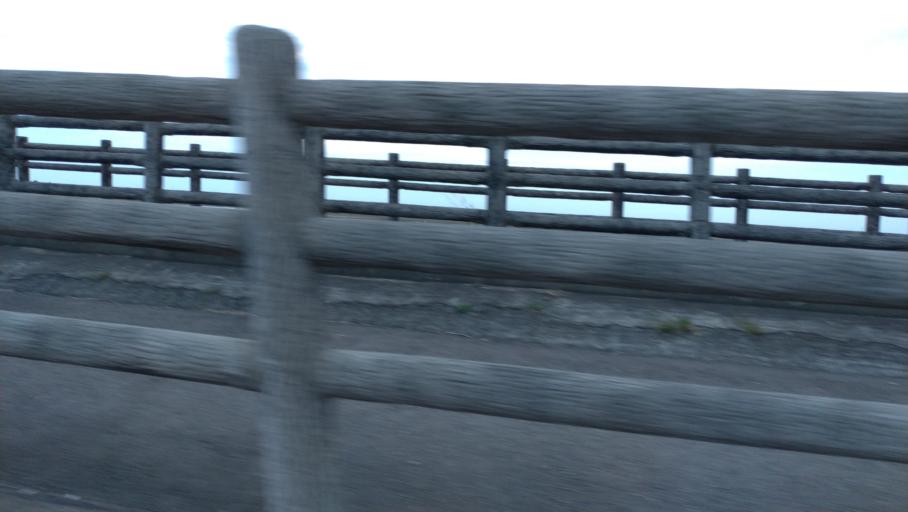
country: TW
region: Taiwan
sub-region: Hsinchu
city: Hsinchu
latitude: 24.7531
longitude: 120.9053
